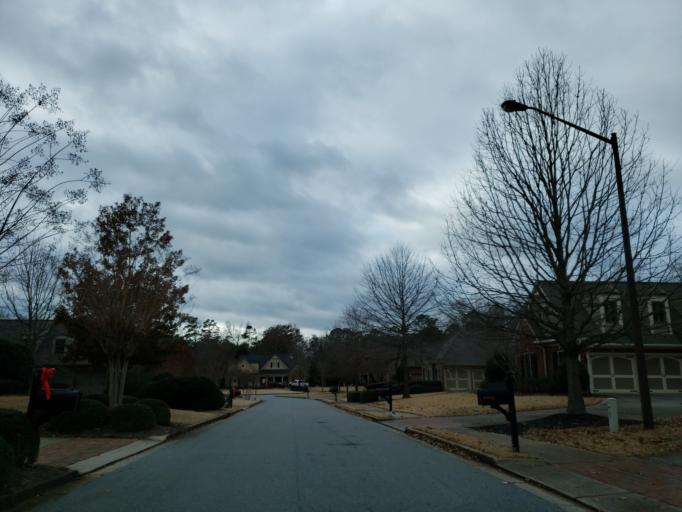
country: US
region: Georgia
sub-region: Cobb County
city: Marietta
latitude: 33.9345
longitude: -84.6124
